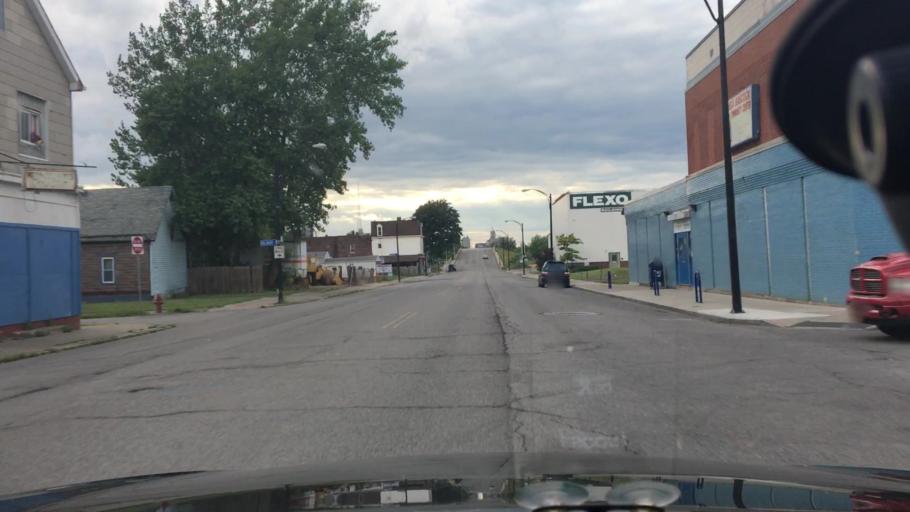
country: US
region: New York
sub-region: Erie County
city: West Seneca
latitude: 42.8709
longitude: -78.8351
